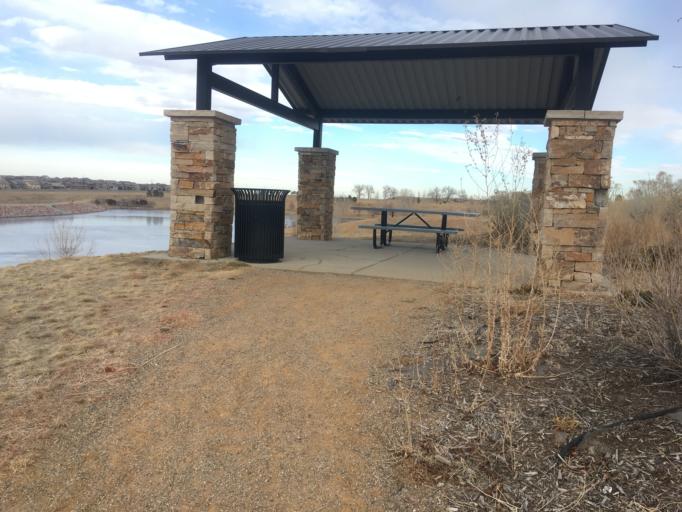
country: US
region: Colorado
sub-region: Boulder County
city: Lafayette
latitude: 39.9795
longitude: -105.0316
